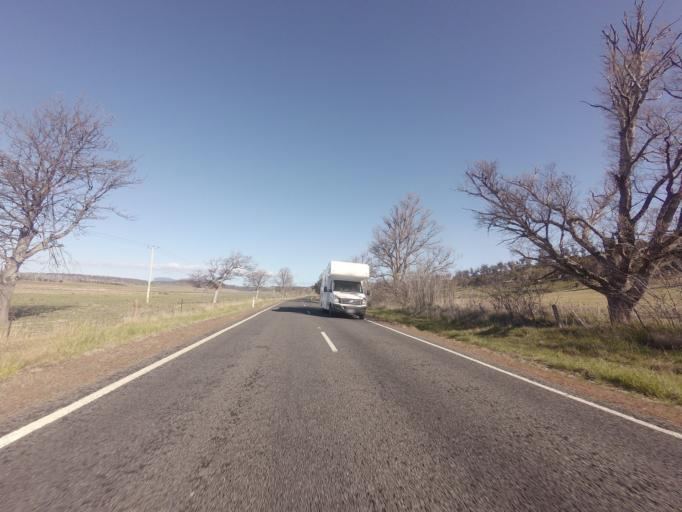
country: AU
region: Tasmania
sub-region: Sorell
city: Sorell
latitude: -42.4791
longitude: 147.9314
